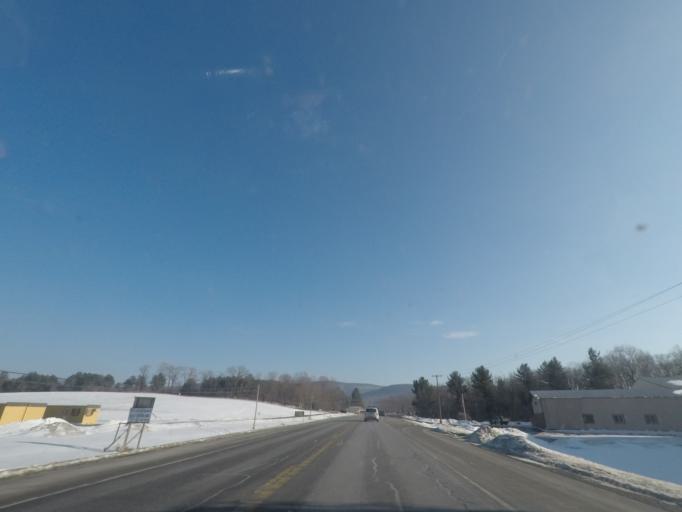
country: US
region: Massachusetts
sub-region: Berkshire County
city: Lanesborough
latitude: 42.5438
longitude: -73.3631
